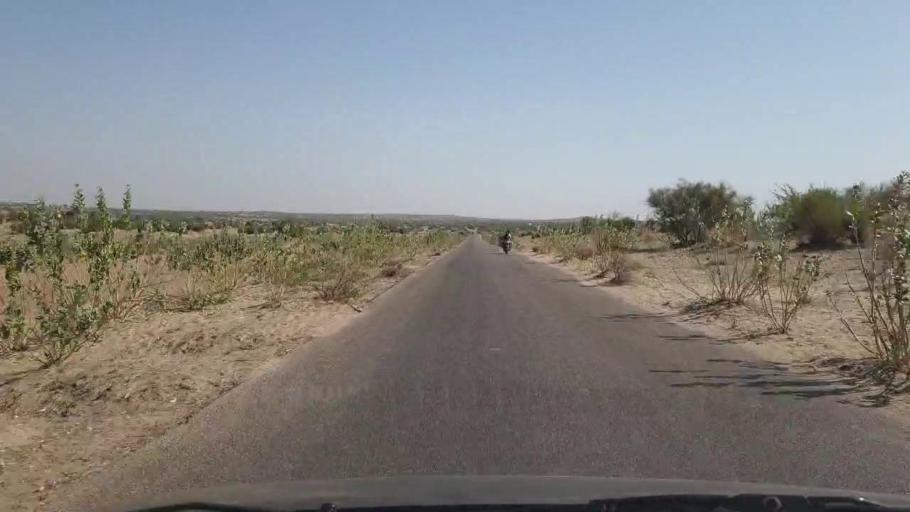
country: PK
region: Sindh
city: Chor
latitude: 25.4925
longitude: 69.8046
